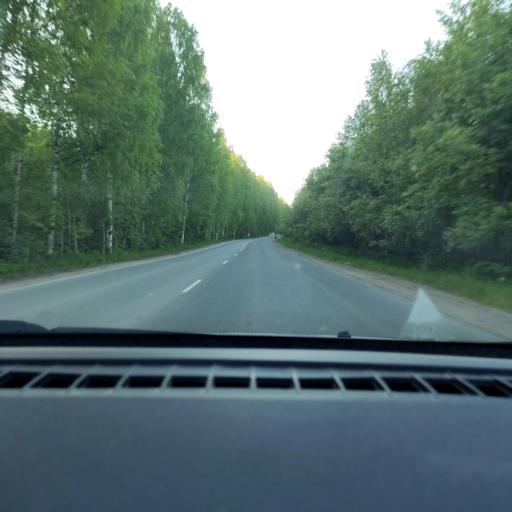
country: RU
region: Perm
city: Polazna
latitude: 58.1200
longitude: 56.4306
